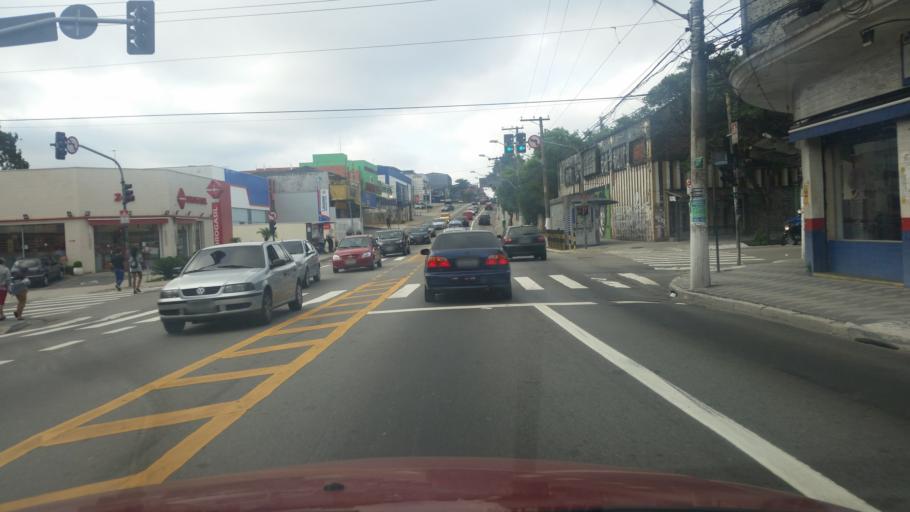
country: BR
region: Sao Paulo
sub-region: Diadema
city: Diadema
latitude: -23.7105
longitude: -46.6994
